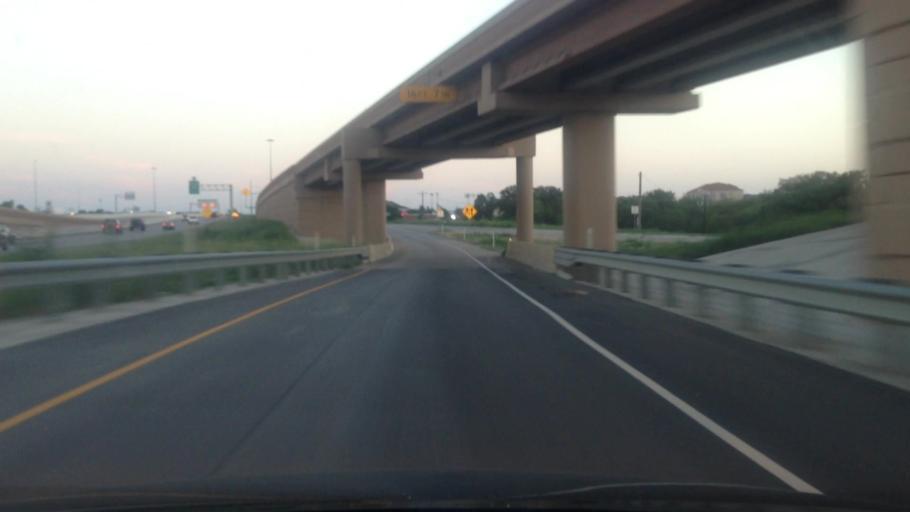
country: US
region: Texas
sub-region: Tarrant County
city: Blue Mound
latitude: 32.8651
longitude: -97.3162
